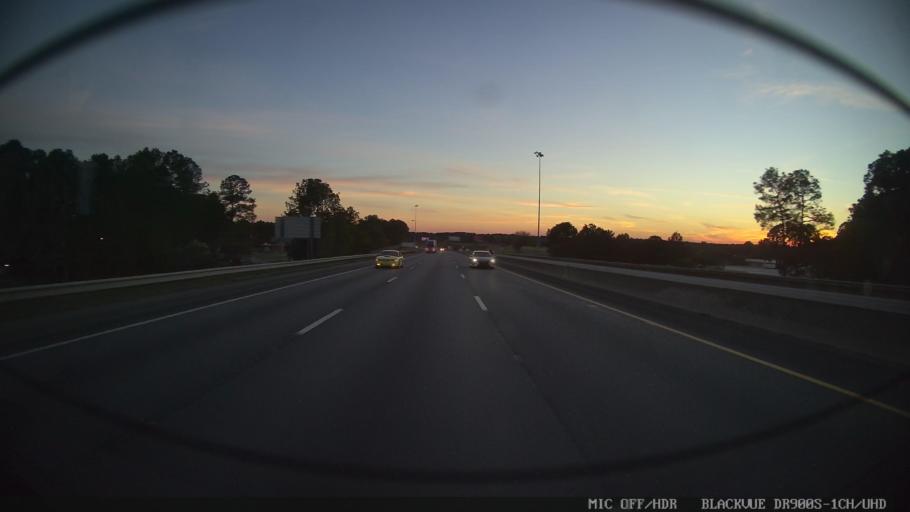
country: US
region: Georgia
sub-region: Tift County
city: Tifton
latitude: 31.4735
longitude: -83.5240
